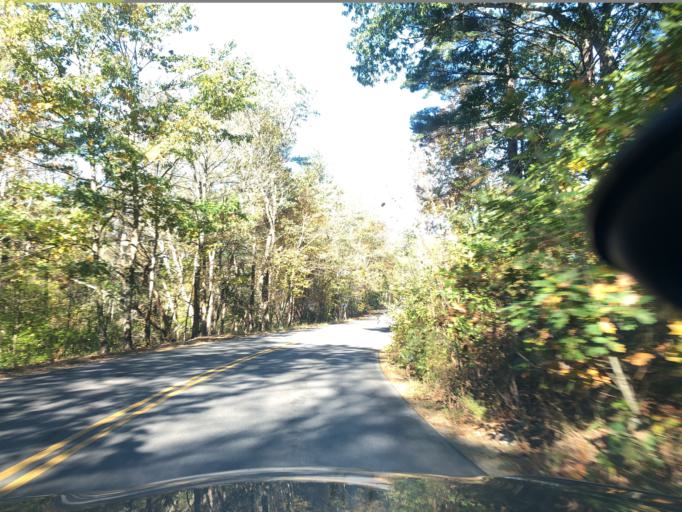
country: US
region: New Hampshire
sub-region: Rockingham County
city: Newmarket
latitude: 43.1044
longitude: -70.9544
